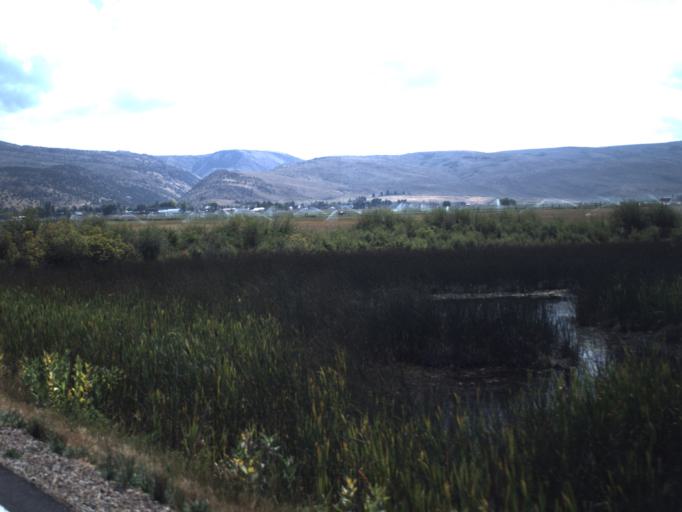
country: US
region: Utah
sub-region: Rich County
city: Randolph
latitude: 41.8361
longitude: -111.3333
